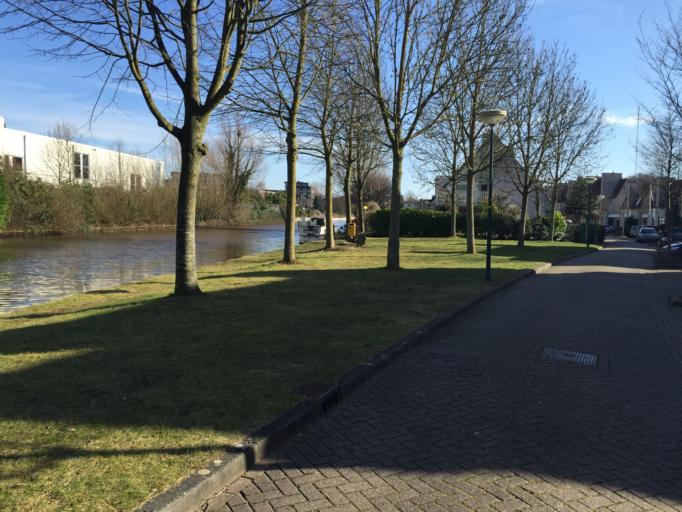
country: NL
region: Utrecht
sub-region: Gemeente IJsselstein
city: IJsselstein
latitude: 52.0256
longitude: 5.0402
